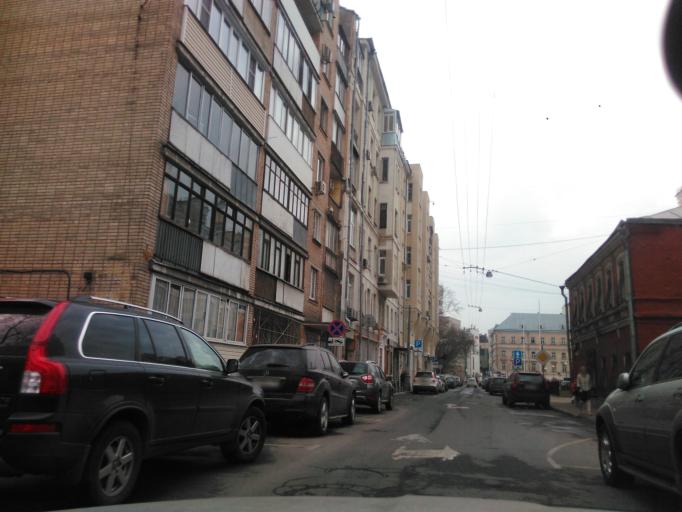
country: RU
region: Moscow
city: Moscow
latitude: 55.7701
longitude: 37.6366
